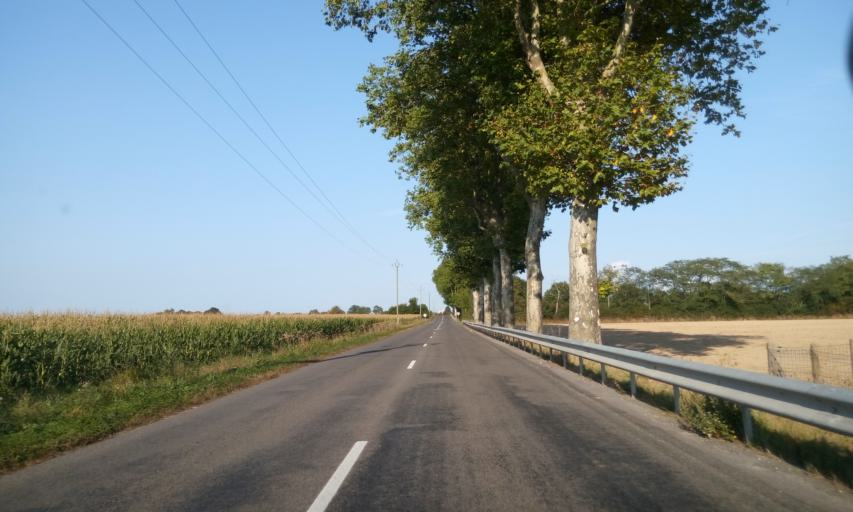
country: FR
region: Rhone-Alpes
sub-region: Departement de l'Ain
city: Villars-les-Dombes
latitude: 45.9972
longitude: 5.0100
